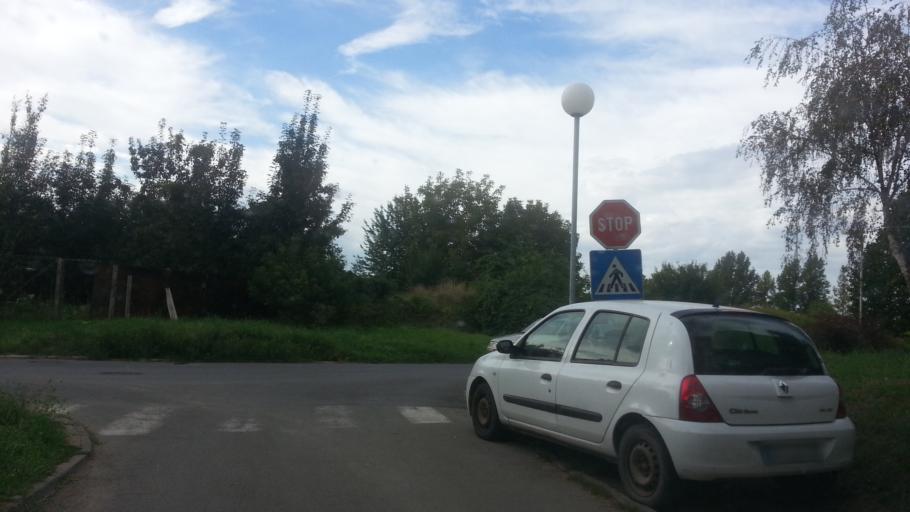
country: RS
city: Novi Banovci
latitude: 44.9682
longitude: 20.2787
